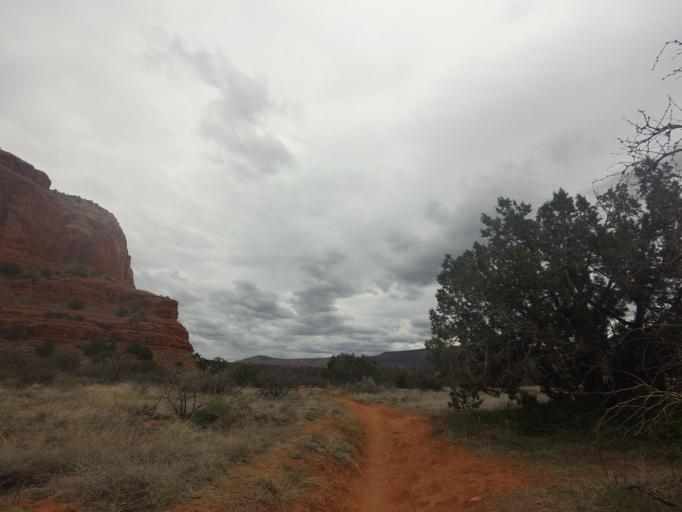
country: US
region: Arizona
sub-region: Yavapai County
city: Village of Oak Creek (Big Park)
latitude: 34.7976
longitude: -111.7585
